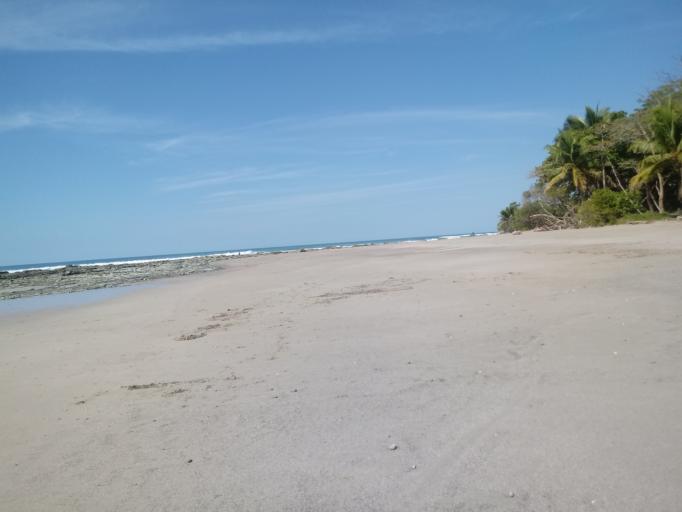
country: CR
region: Guanacaste
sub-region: Canton de Nandayure
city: Bejuco
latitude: 9.6688
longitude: -85.1956
